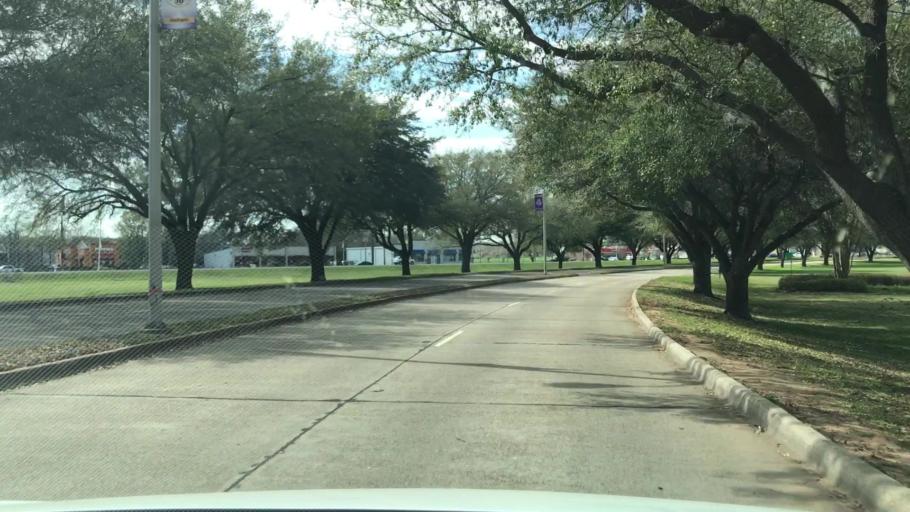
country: US
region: Louisiana
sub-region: Bossier Parish
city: Bossier City
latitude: 32.4255
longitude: -93.7063
